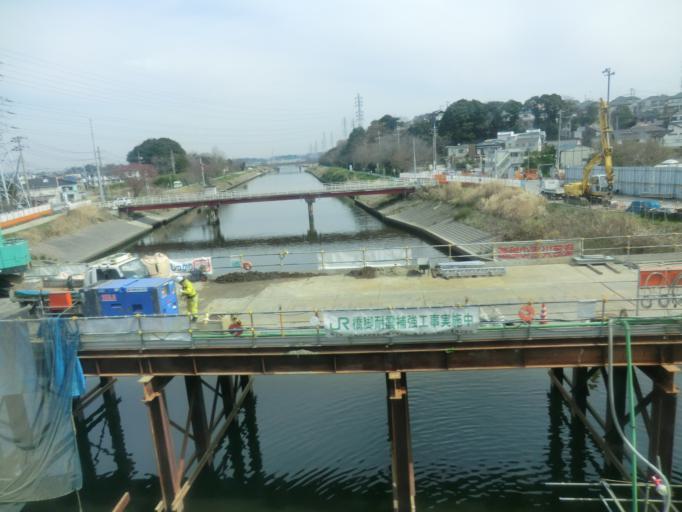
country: JP
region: Chiba
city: Chiba
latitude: 35.6558
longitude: 140.0633
